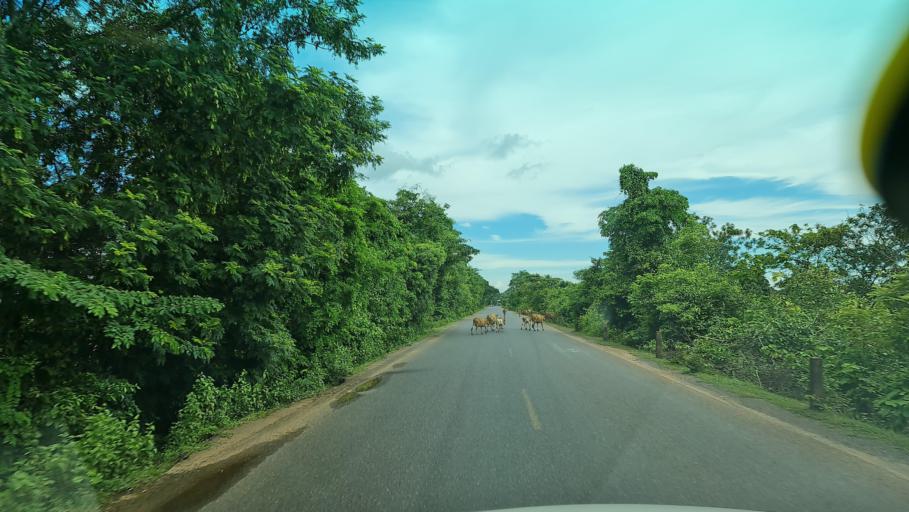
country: TH
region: Nakhon Phanom
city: Ban Phaeng
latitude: 18.0717
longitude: 104.2966
